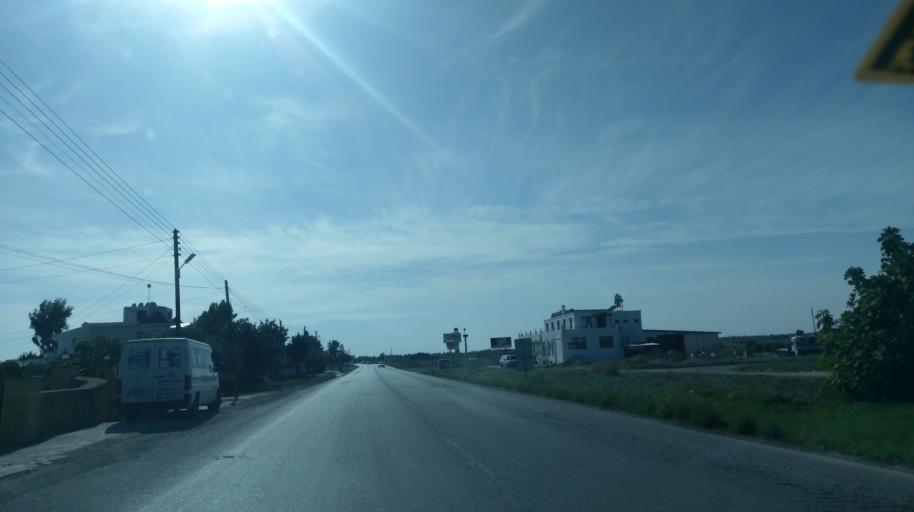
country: CY
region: Ammochostos
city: Trikomo
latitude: 35.2999
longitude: 33.9381
